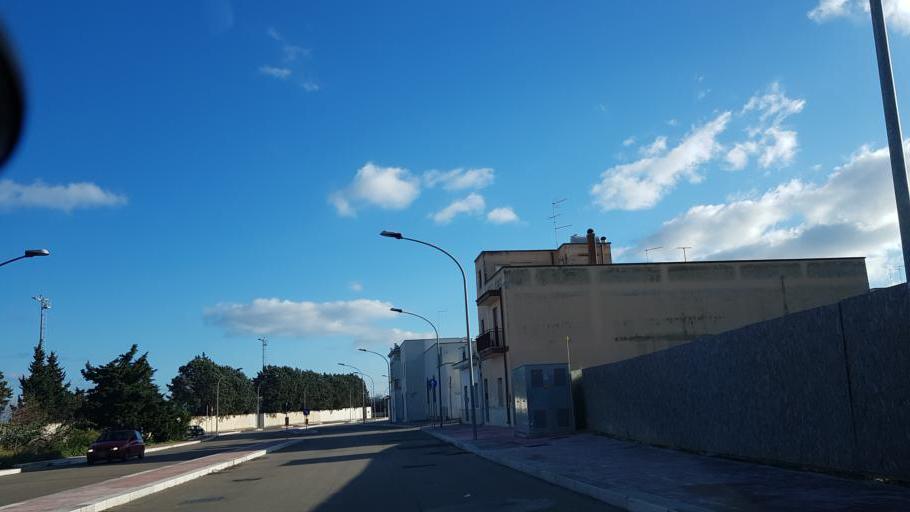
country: IT
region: Apulia
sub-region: Provincia di Brindisi
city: Brindisi
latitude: 40.6478
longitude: 17.9206
